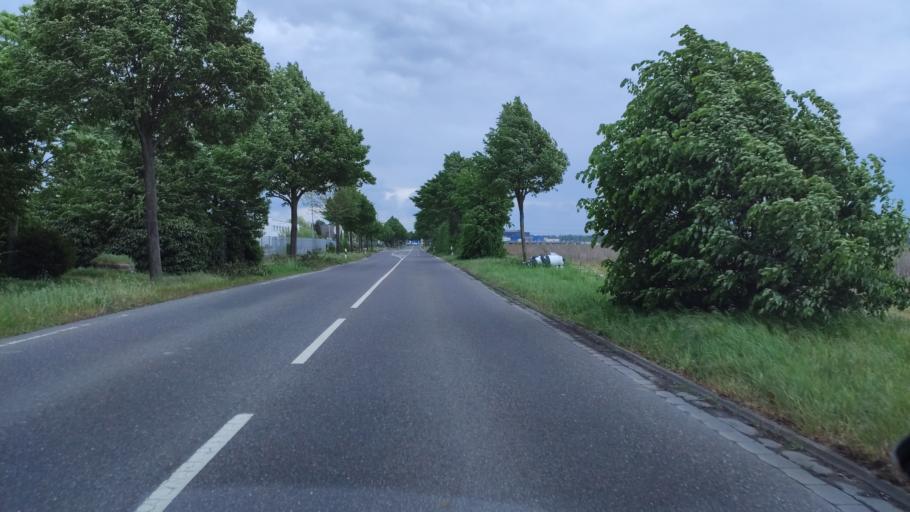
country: DE
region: North Rhine-Westphalia
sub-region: Regierungsbezirk Dusseldorf
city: Kaarst
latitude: 51.2113
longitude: 6.6273
